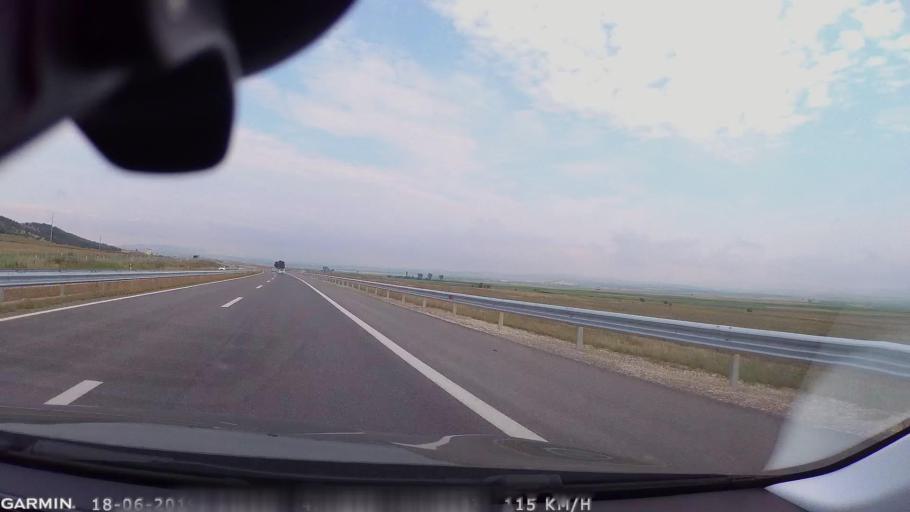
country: MK
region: Sveti Nikole
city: Sveti Nikole
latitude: 41.8067
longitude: 22.0654
